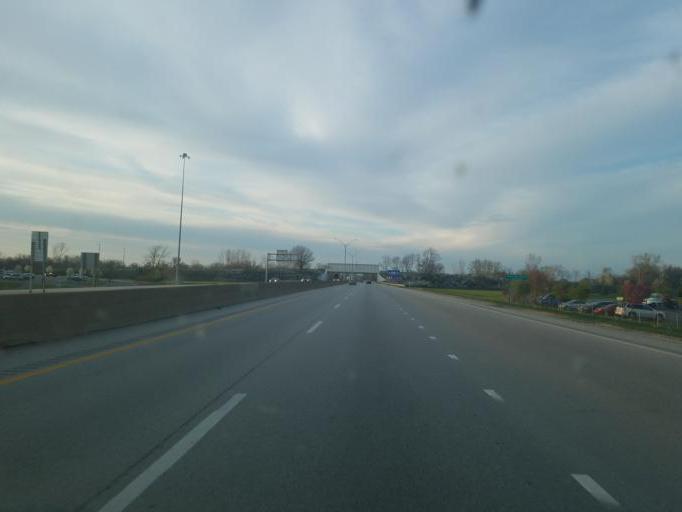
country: US
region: Ohio
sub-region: Wood County
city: Northwood
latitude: 41.6198
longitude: -83.4769
